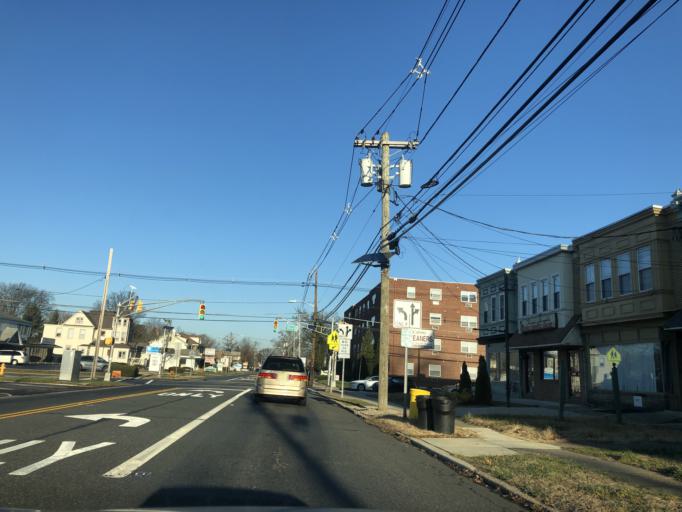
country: US
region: New Jersey
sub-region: Camden County
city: Audubon
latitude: 39.8910
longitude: -75.0653
